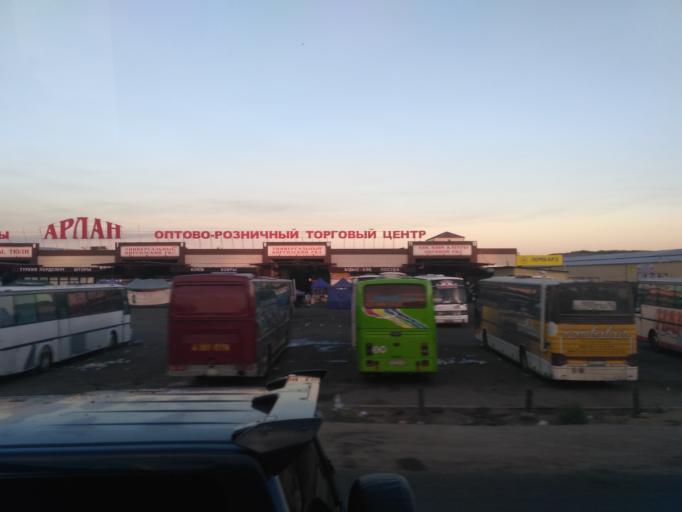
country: KZ
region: Almaty Oblysy
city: Burunday
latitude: 43.3209
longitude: 76.9049
